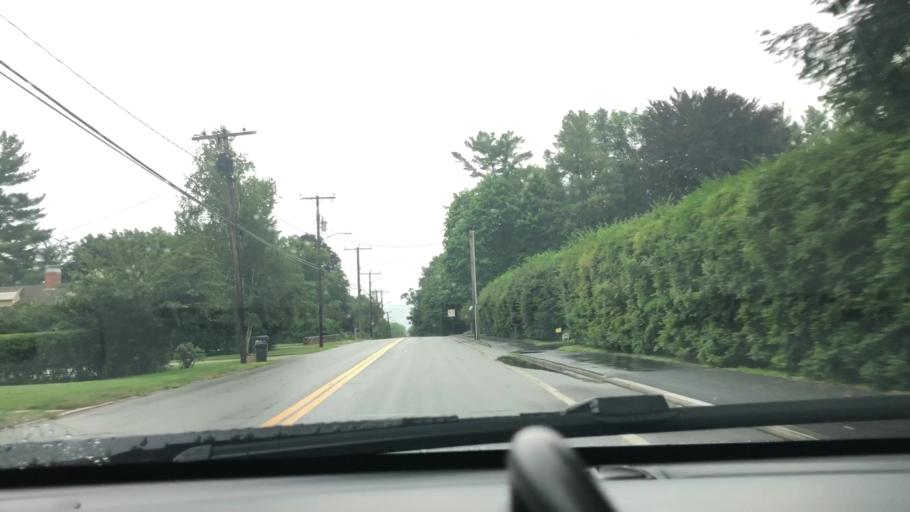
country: US
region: New Hampshire
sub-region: Hillsborough County
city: Manchester
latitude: 43.0198
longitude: -71.4622
